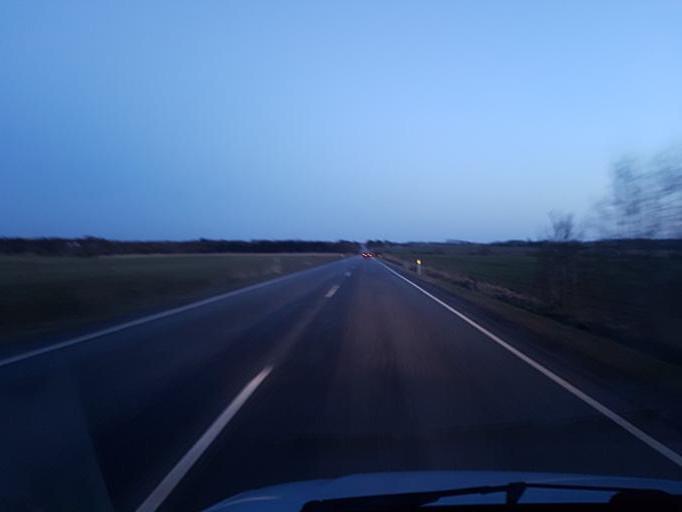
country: DK
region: Central Jutland
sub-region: Ringkobing-Skjern Kommune
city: Skjern
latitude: 56.0701
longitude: 8.5062
